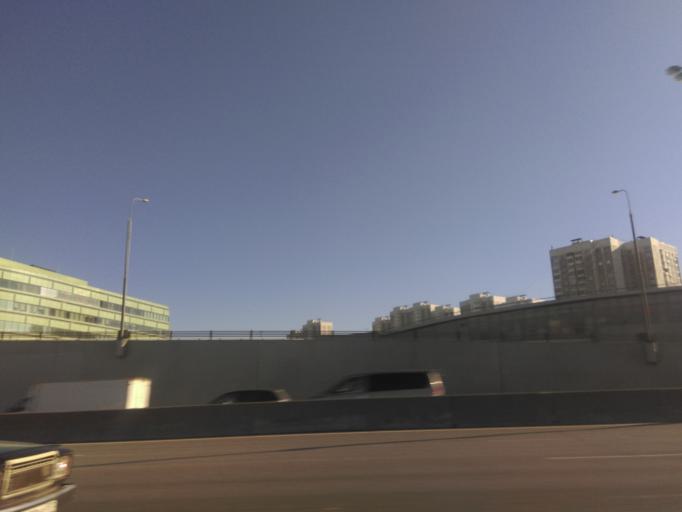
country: RU
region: Moskovskaya
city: Marfino
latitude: 55.7104
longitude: 37.3879
